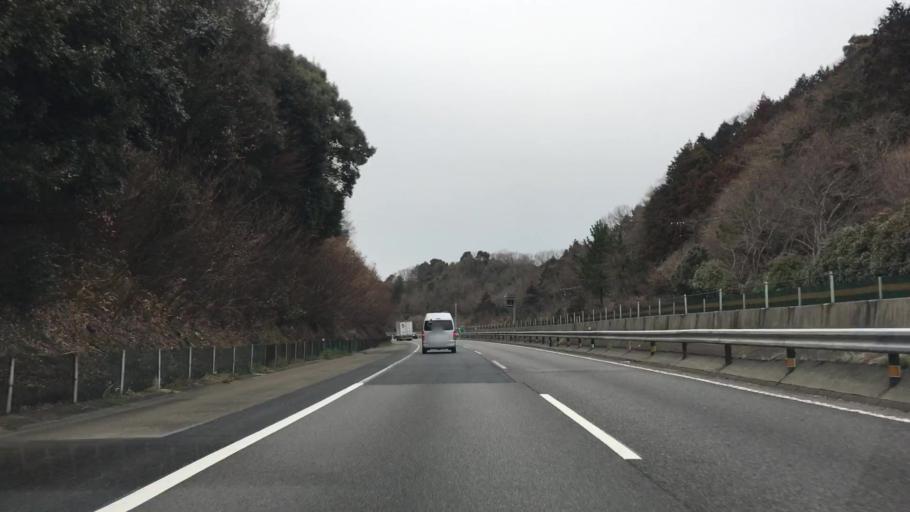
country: JP
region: Aichi
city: Gamagori
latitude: 34.8988
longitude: 137.2564
